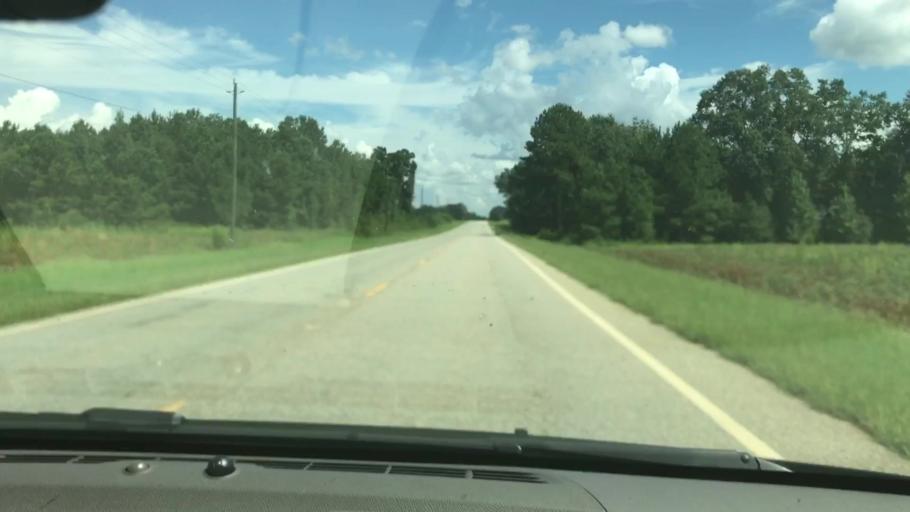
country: US
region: Georgia
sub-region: Quitman County
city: Georgetown
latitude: 31.7583
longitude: -85.0684
